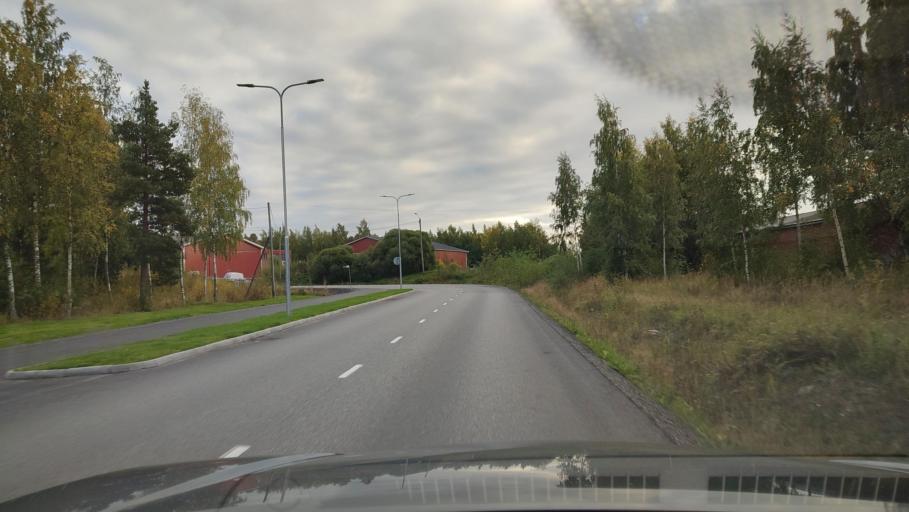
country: FI
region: Ostrobothnia
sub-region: Sydosterbotten
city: Kristinestad
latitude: 62.2635
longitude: 21.3834
